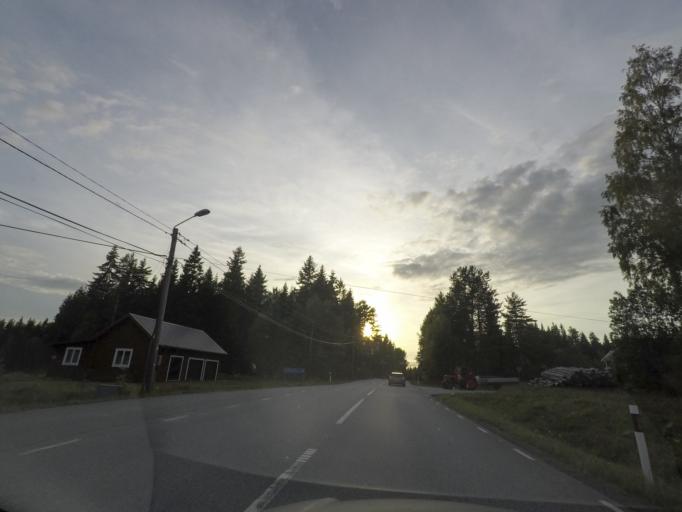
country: SE
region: OErebro
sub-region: Nora Kommun
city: As
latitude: 59.5189
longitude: 14.9106
